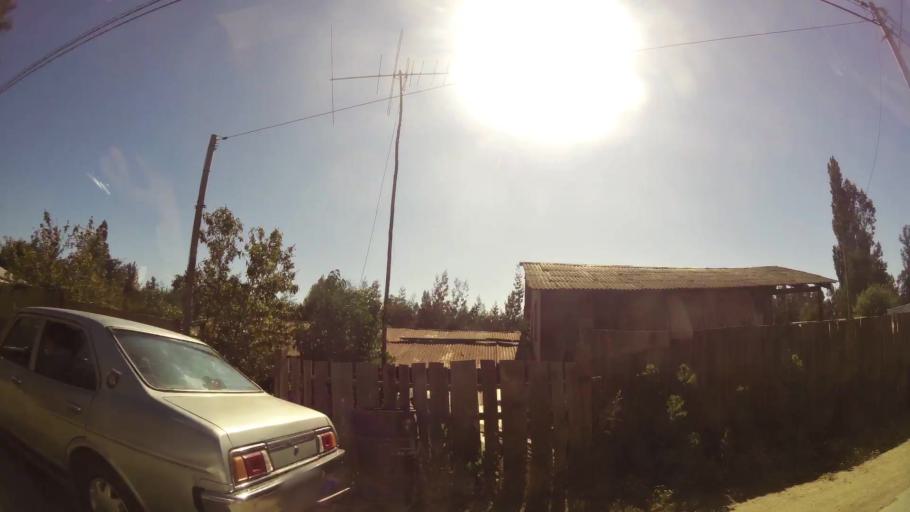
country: CL
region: Valparaiso
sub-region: Provincia de Valparaiso
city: Vina del Mar
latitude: -33.1504
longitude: -71.5603
